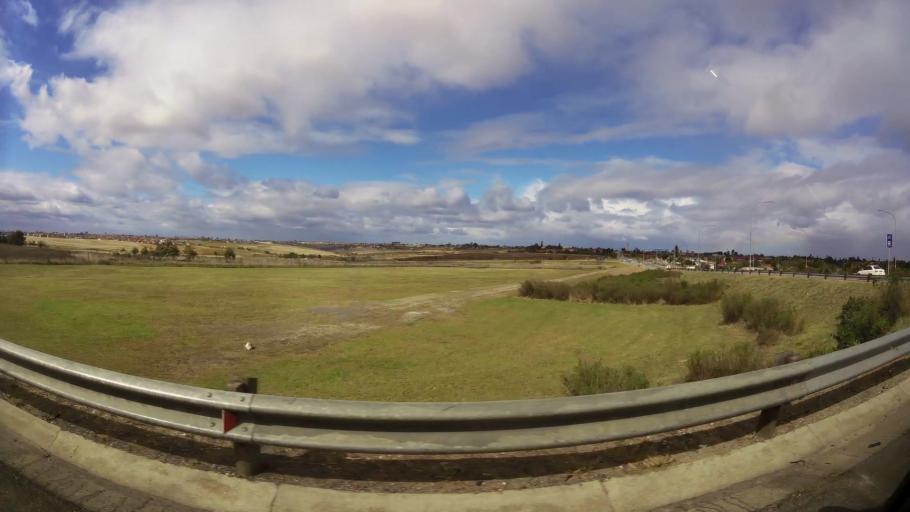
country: ZA
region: Western Cape
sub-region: Eden District Municipality
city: George
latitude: -33.9993
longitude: 22.4460
